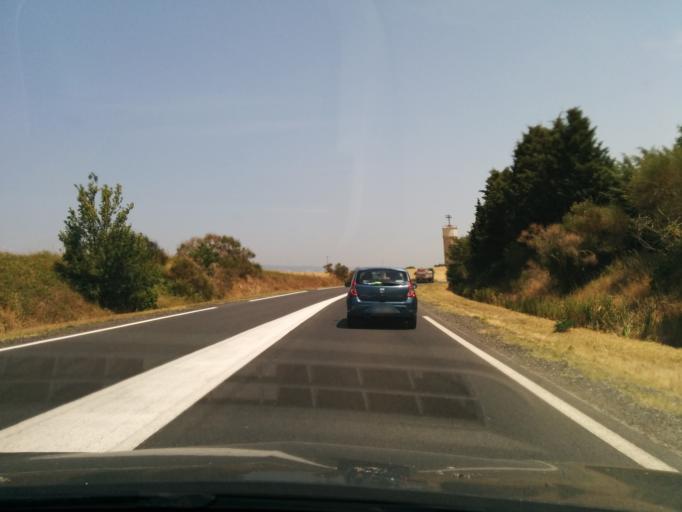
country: FR
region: Midi-Pyrenees
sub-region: Departement de la Haute-Garonne
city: Avignonet-Lauragais
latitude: 43.3496
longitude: 1.8488
